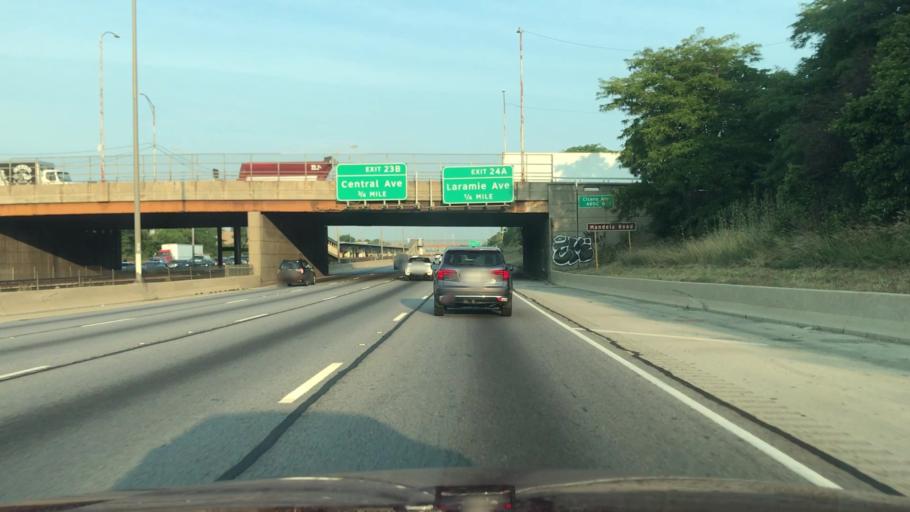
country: US
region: Illinois
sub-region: Cook County
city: Cicero
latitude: 41.8718
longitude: -87.7440
